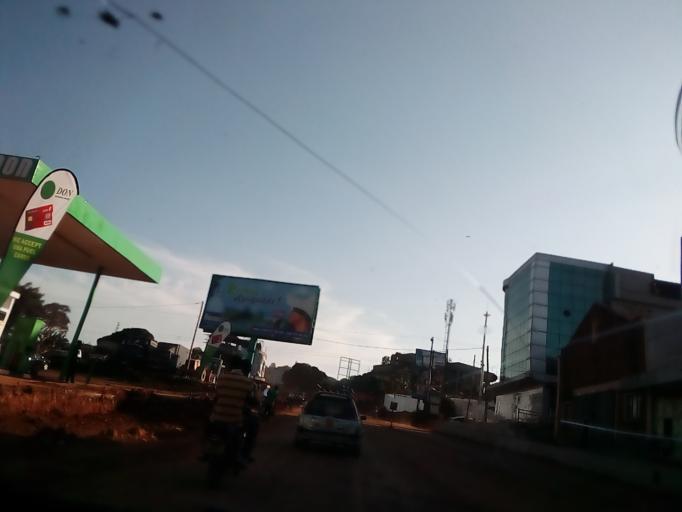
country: UG
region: Central Region
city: Masaka
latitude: -0.3333
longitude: 31.7434
